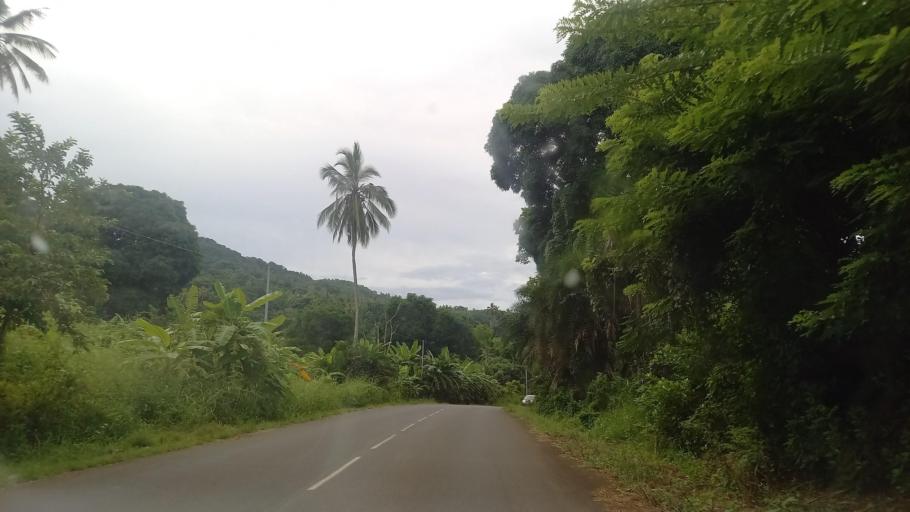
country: YT
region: Boueni
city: Boueni
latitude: -12.9198
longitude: 45.1017
